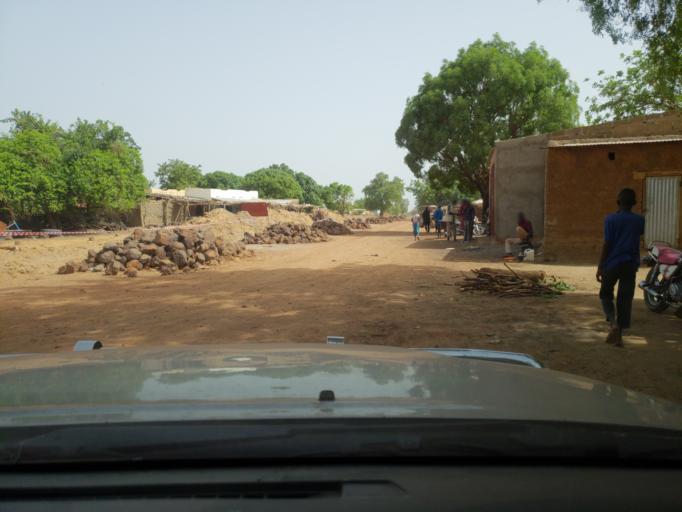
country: ML
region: Koulikoro
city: Kati
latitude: 12.9526
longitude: -8.1756
